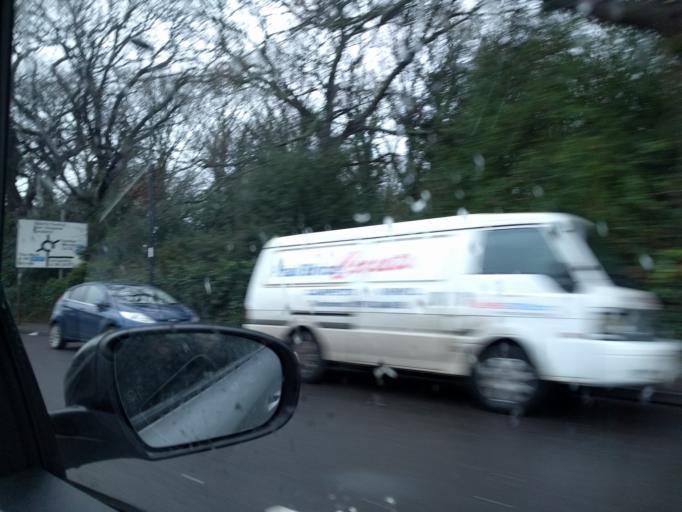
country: GB
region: England
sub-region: Southampton
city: Southampton
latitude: 50.9331
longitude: -1.4181
